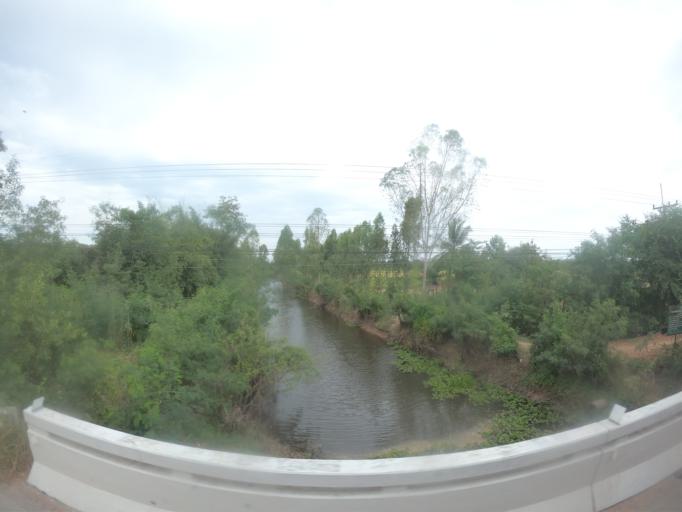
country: TH
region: Maha Sarakham
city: Kantharawichai
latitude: 16.3357
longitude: 103.2300
